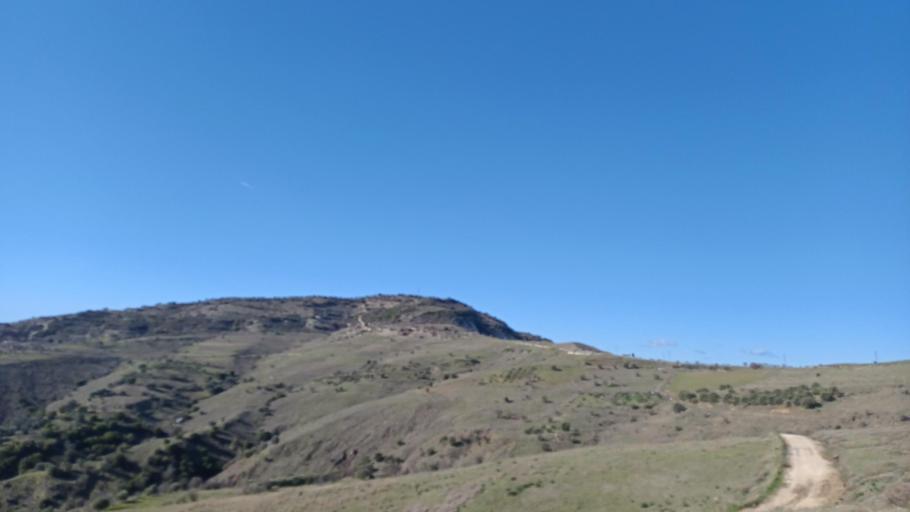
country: CY
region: Limassol
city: Pachna
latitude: 34.8220
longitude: 32.6884
